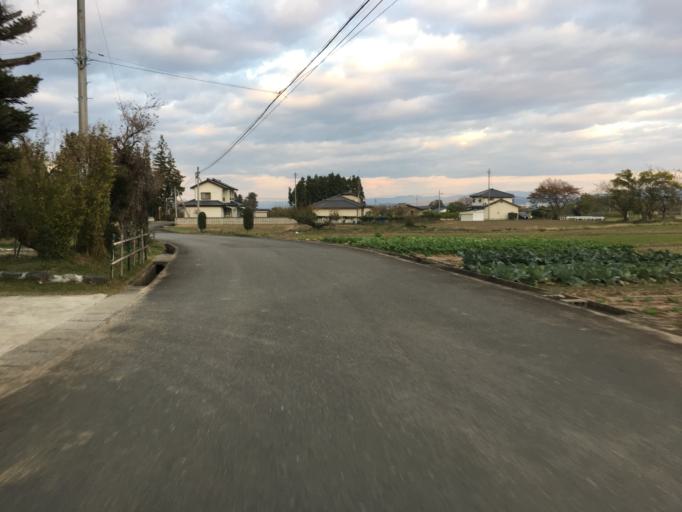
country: JP
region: Fukushima
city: Fukushima-shi
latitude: 37.7400
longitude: 140.3848
